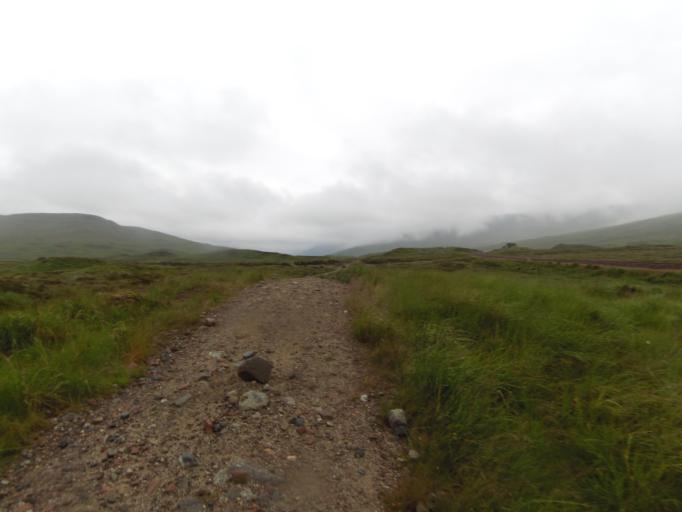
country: GB
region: Scotland
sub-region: Highland
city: Spean Bridge
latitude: 56.7631
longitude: -4.6964
